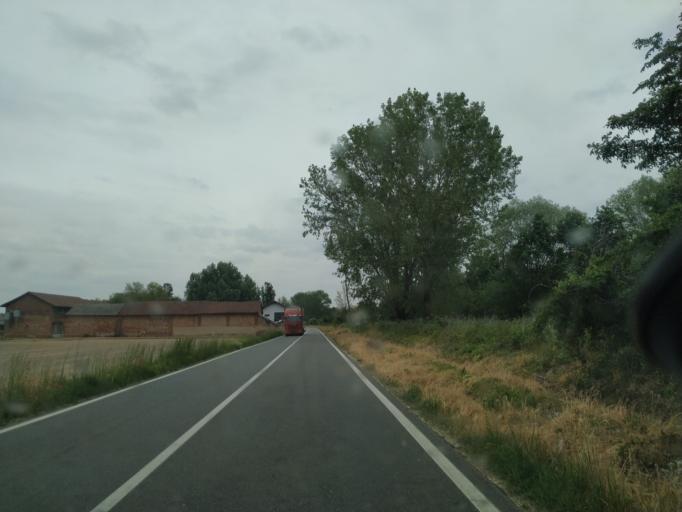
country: IT
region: Piedmont
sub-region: Provincia di Vercelli
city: Caresanablot
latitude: 45.3340
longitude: 8.3929
